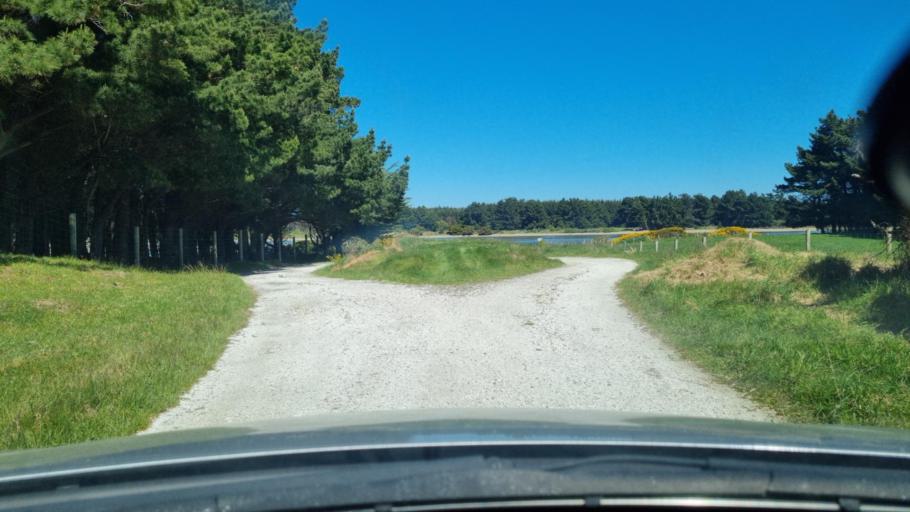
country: NZ
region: Southland
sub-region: Invercargill City
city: Invercargill
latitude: -46.4584
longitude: 168.2703
